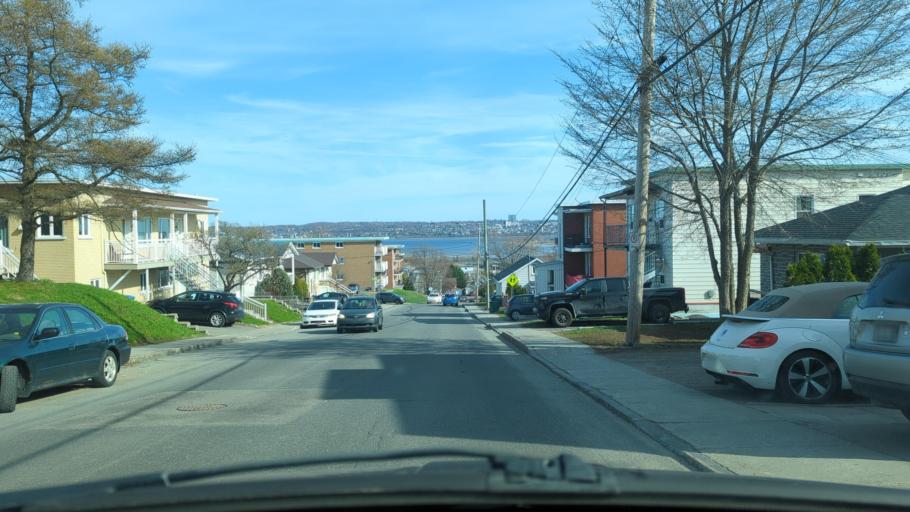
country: CA
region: Quebec
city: Quebec
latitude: 46.8559
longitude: -71.2068
